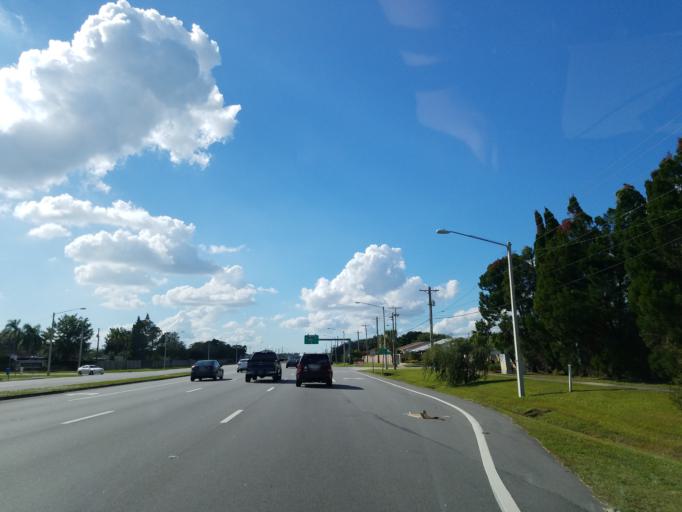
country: US
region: Florida
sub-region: Hillsborough County
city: Brandon
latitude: 27.9234
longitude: -82.3123
